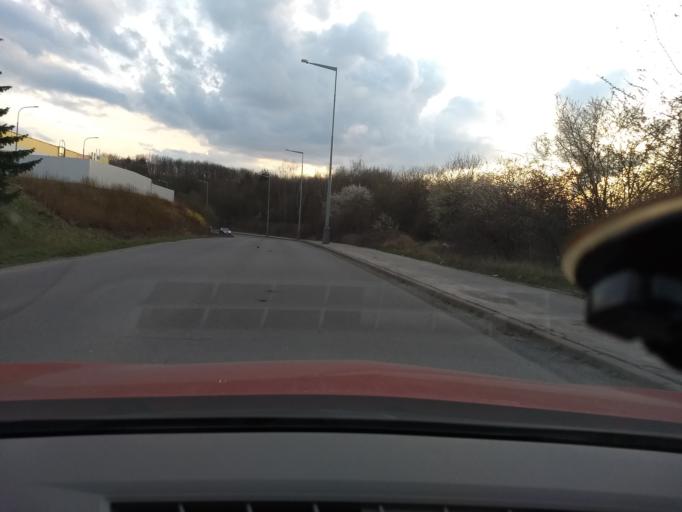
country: CZ
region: Central Bohemia
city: Hostivice
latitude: 50.0550
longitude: 14.3084
